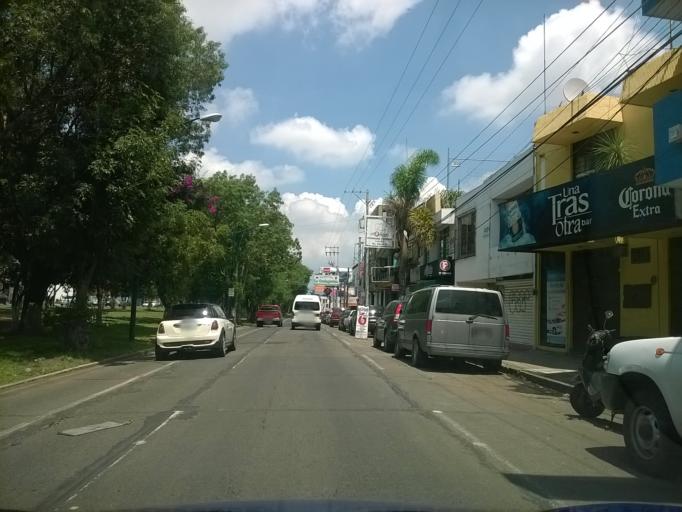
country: MX
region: Michoacan
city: Morelia
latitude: 19.6890
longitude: -101.1657
